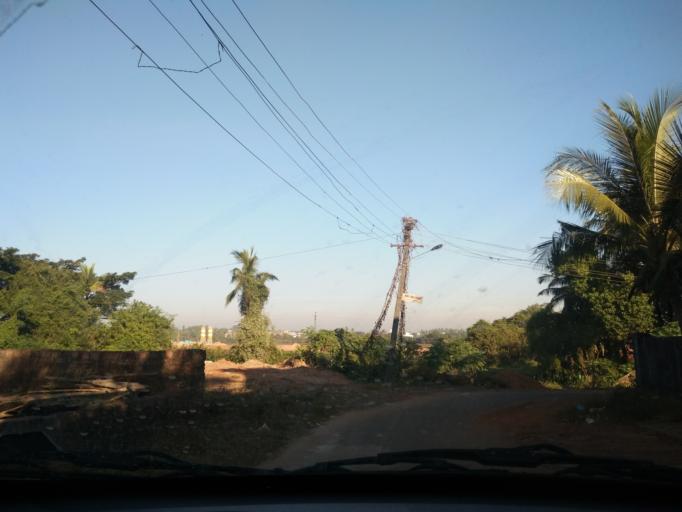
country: IN
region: Goa
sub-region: South Goa
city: Madgaon
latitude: 15.2578
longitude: 73.9543
